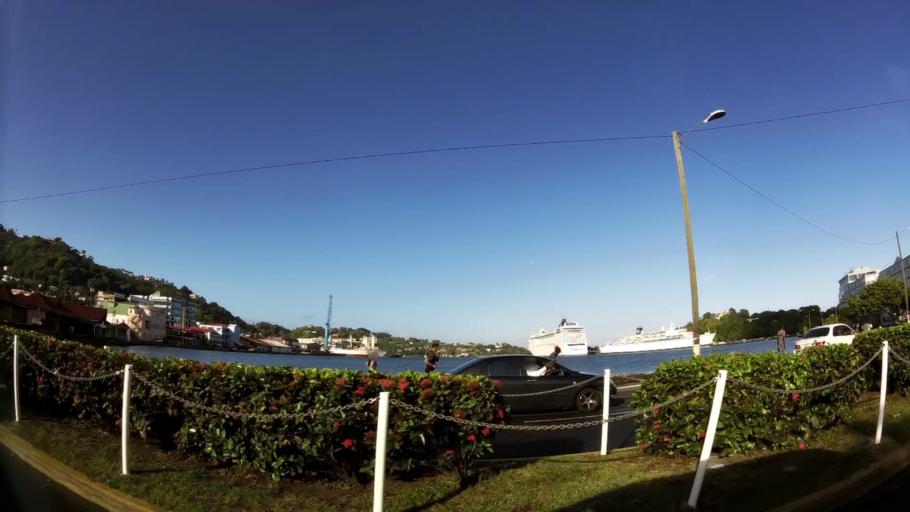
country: LC
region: Castries Quarter
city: Bisee
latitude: 14.0123
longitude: -60.9896
